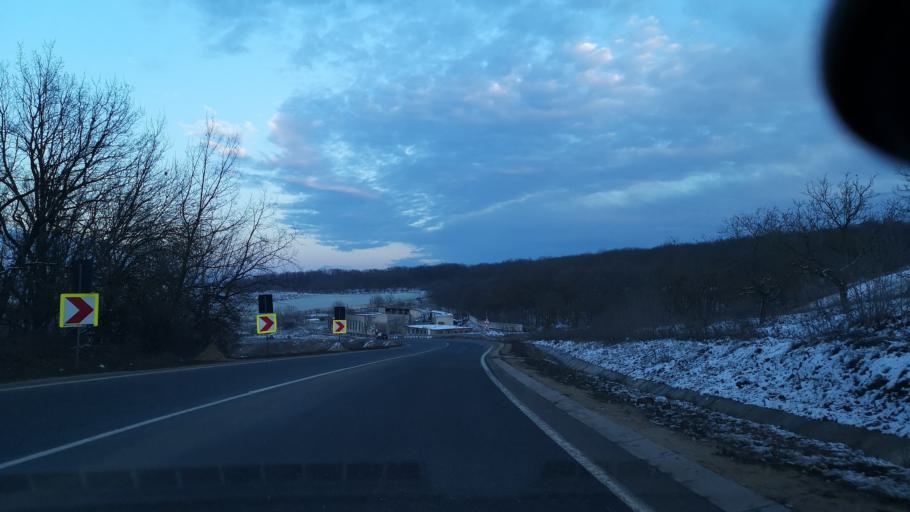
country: MD
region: Rezina
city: Saharna
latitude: 47.5969
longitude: 28.8272
